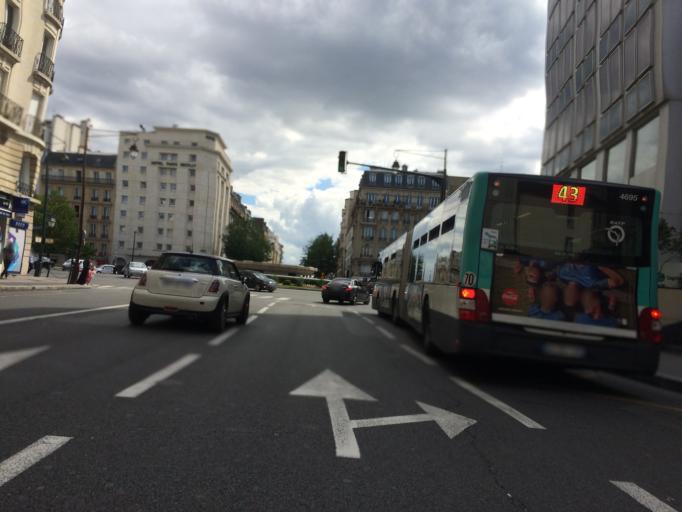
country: FR
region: Ile-de-France
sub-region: Departement des Hauts-de-Seine
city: Neuilly-sur-Seine
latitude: 48.8853
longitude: 2.2607
